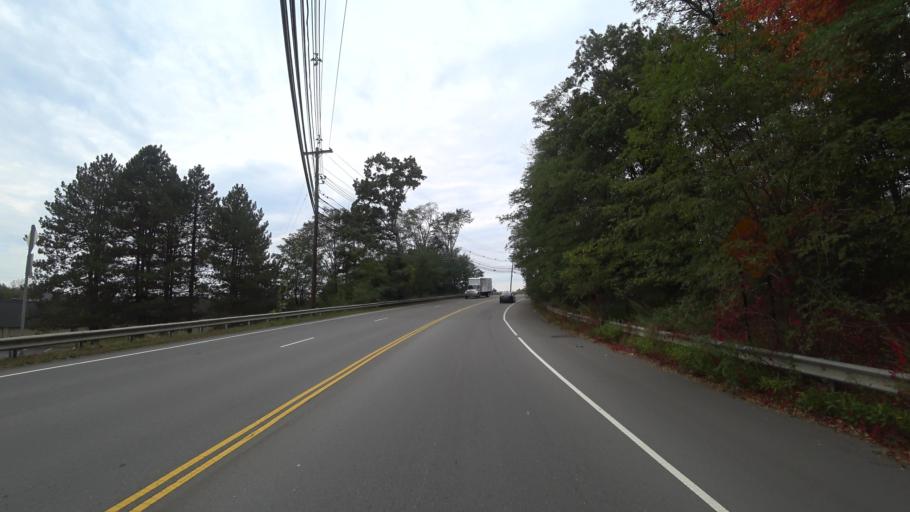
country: US
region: Massachusetts
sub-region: Middlesex County
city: Wilmington
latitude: 42.5911
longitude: -71.1601
